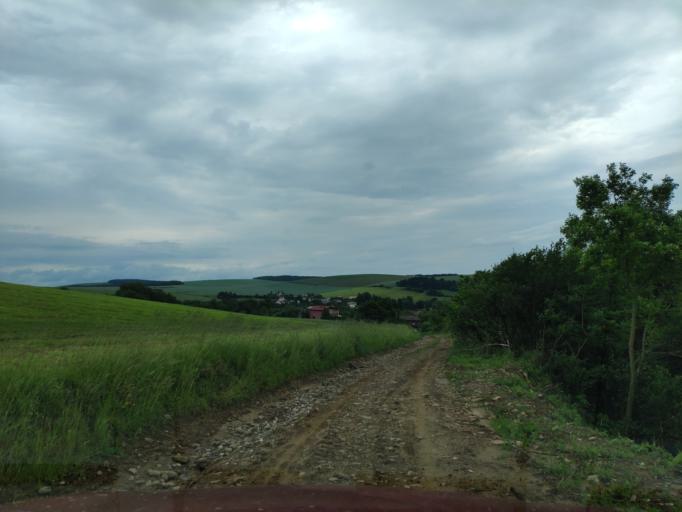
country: SK
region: Presovsky
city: Sabinov
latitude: 49.0504
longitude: 21.0090
